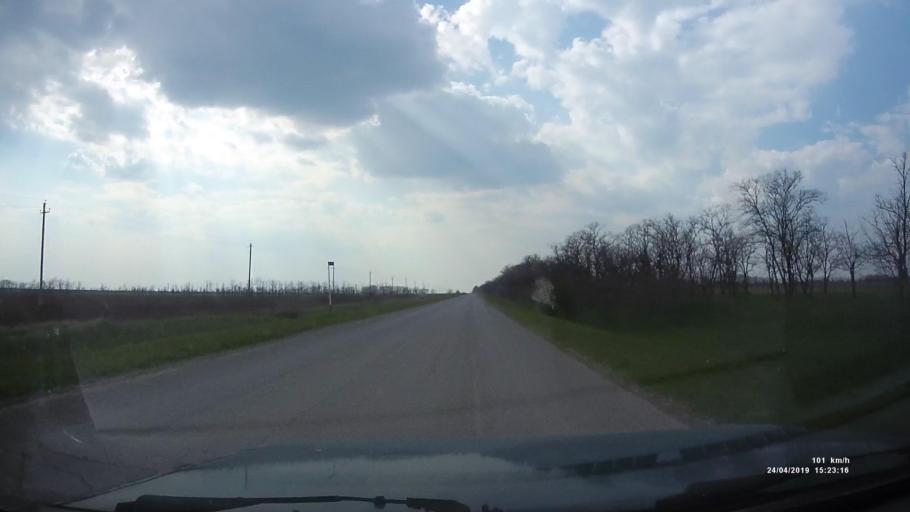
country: RU
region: Rostov
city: Remontnoye
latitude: 46.5426
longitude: 43.0934
